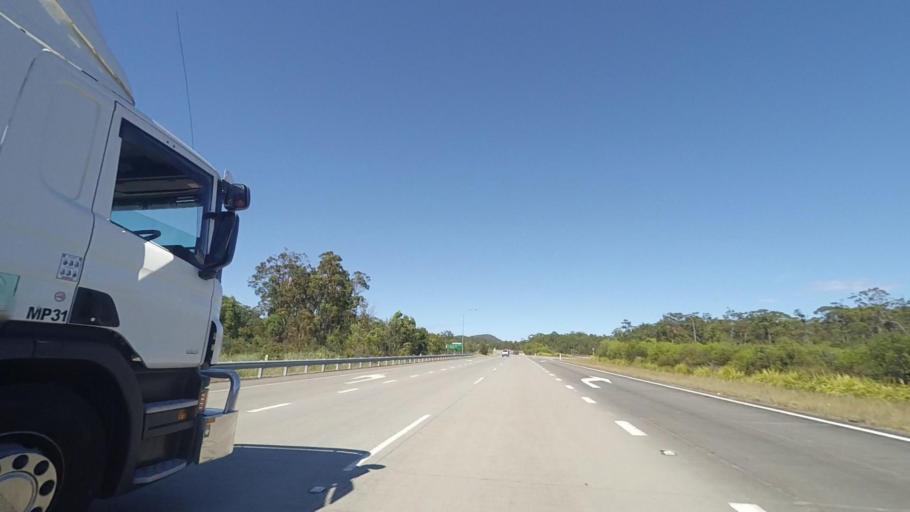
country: AU
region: New South Wales
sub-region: Port Stephens Shire
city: Port Stephens
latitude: -32.6242
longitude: 152.0605
